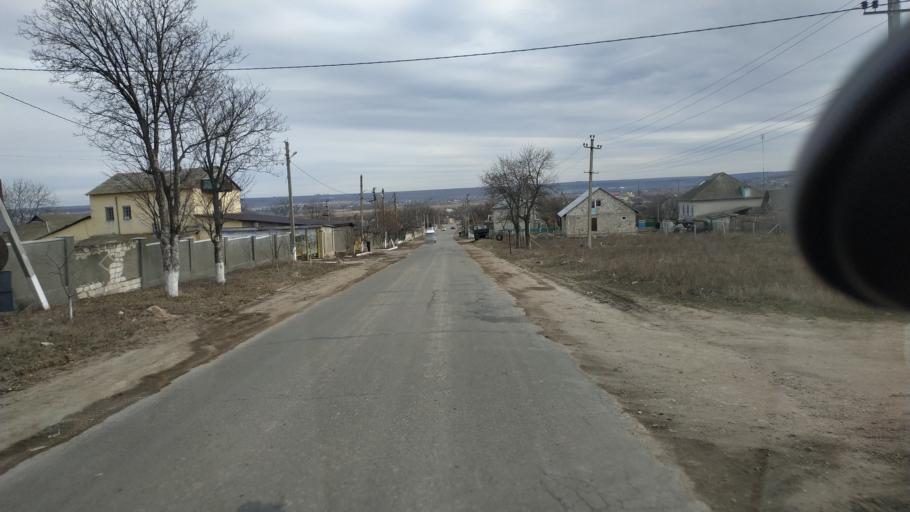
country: MD
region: Telenesti
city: Dubasari
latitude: 47.2608
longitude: 29.1202
